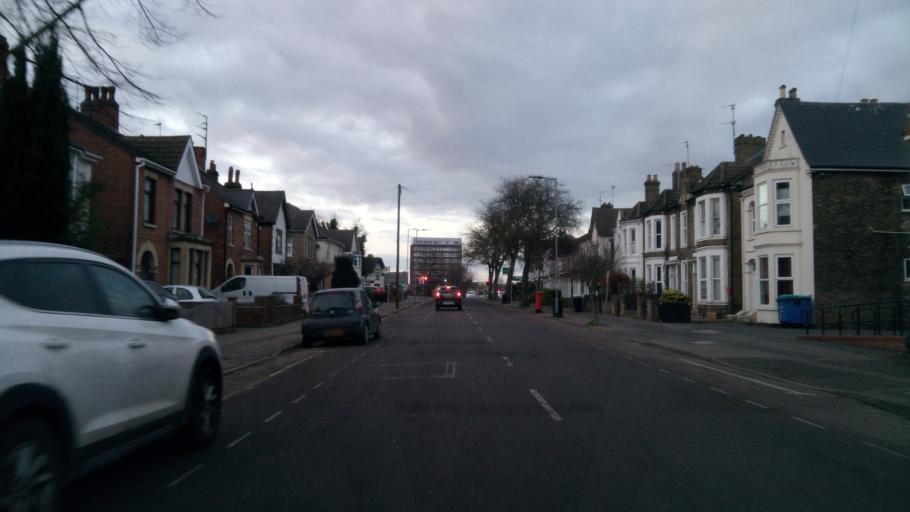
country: GB
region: England
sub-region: Peterborough
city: Peterborough
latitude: 52.5627
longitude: -0.2421
